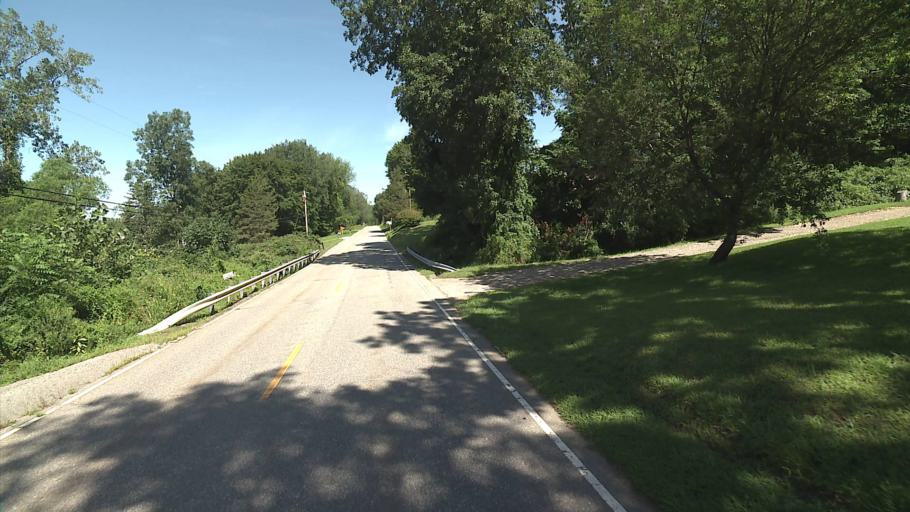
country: US
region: Connecticut
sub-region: New London County
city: Baltic
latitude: 41.6449
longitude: -72.0899
